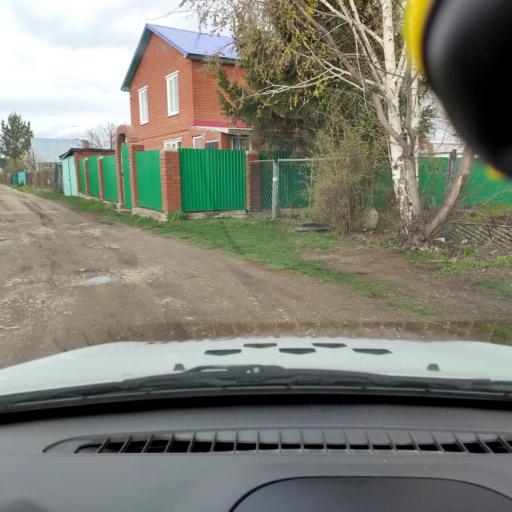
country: RU
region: Samara
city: Tol'yatti
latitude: 53.5815
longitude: 49.3154
